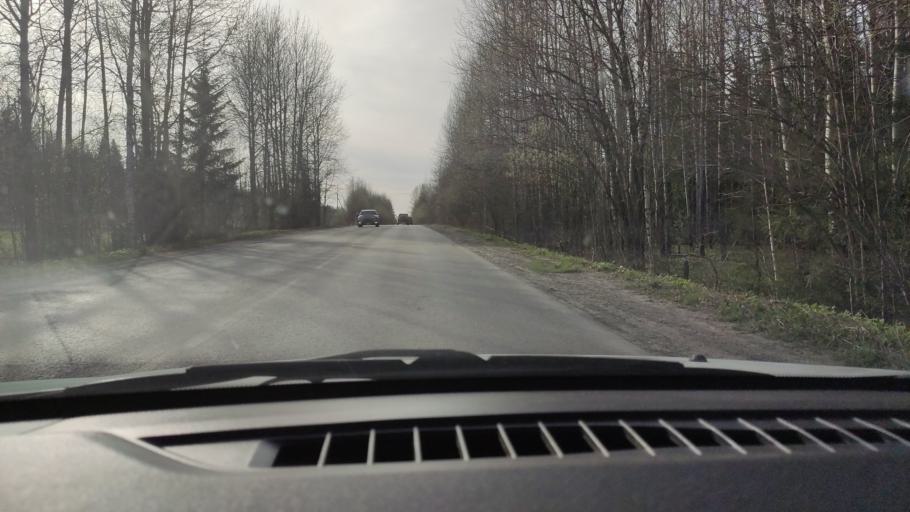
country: RU
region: Perm
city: Ferma
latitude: 57.9376
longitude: 56.4601
